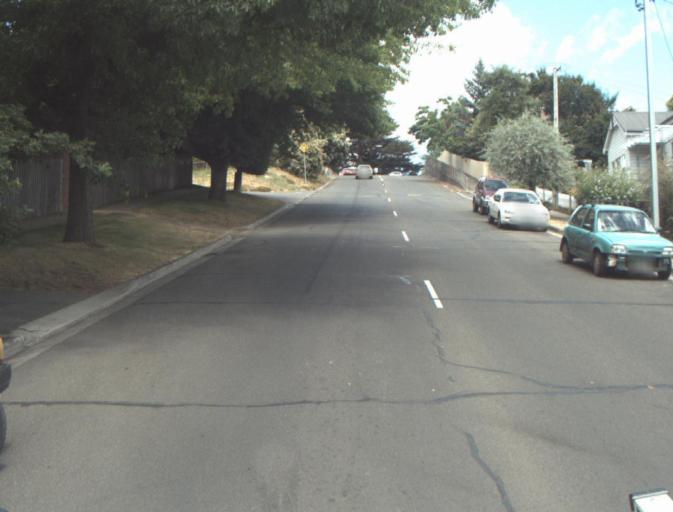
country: AU
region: Tasmania
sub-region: Launceston
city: East Launceston
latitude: -41.4452
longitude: 147.1525
